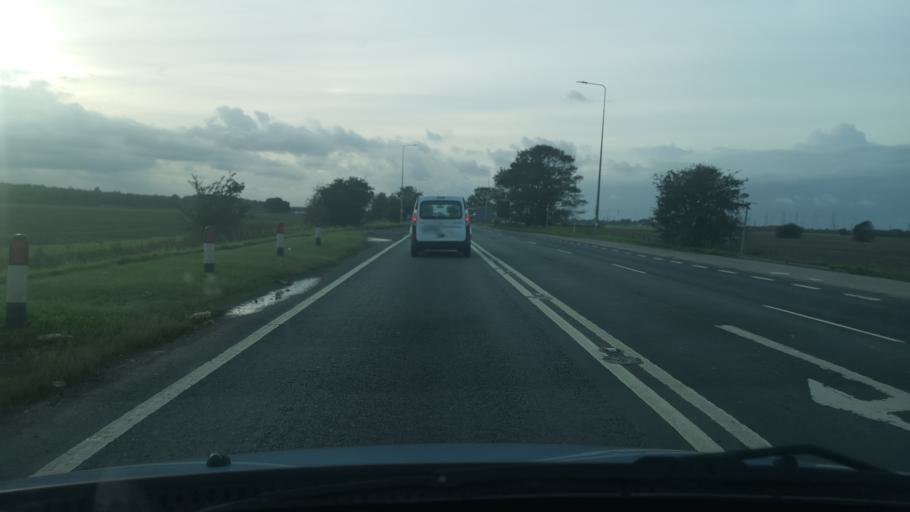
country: GB
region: England
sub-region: North Lincolnshire
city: Gunness
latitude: 53.5895
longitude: -0.7014
